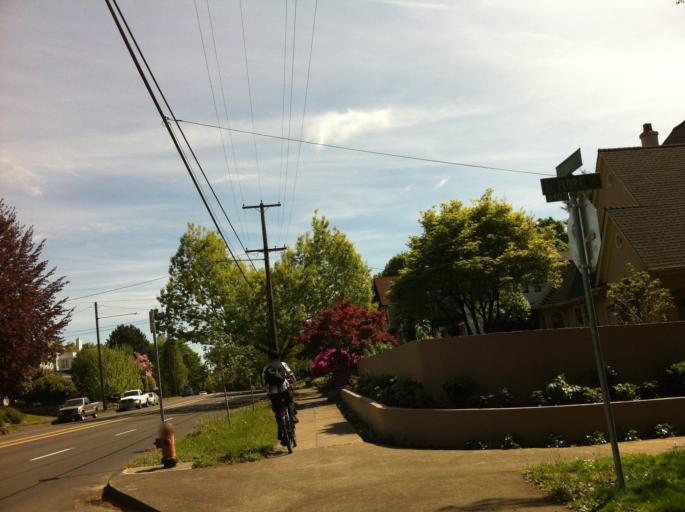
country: US
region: Oregon
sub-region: Multnomah County
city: Portland
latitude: 45.5228
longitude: -122.6287
